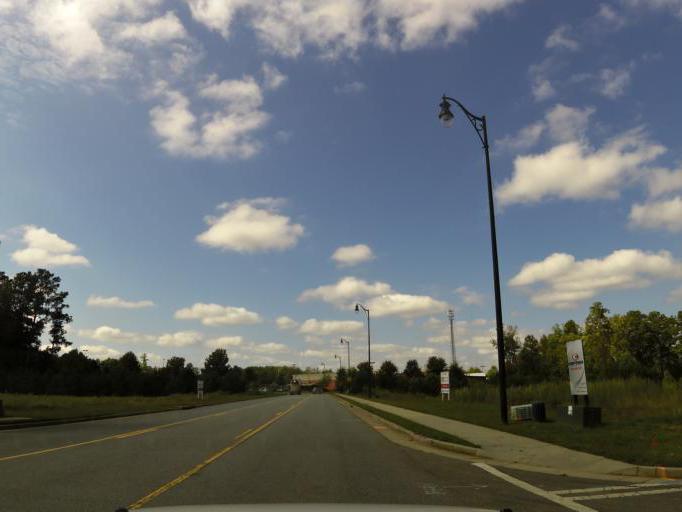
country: US
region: Georgia
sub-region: Cobb County
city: Acworth
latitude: 34.0380
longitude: -84.6777
